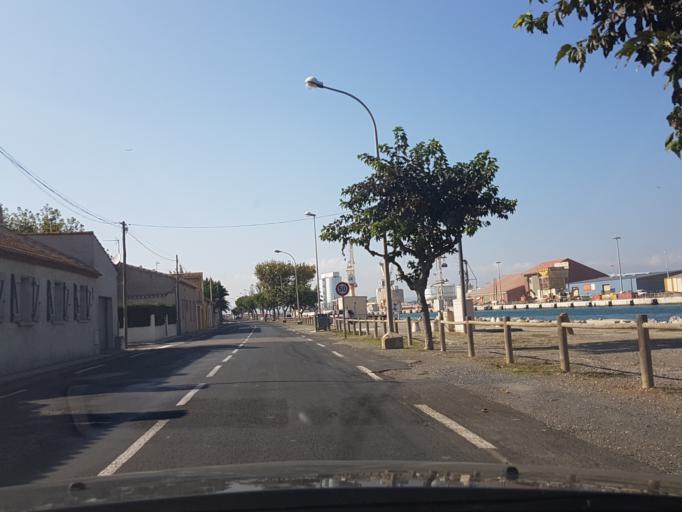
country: FR
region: Languedoc-Roussillon
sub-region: Departement de l'Aude
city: Port-la-Nouvelle
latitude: 43.0191
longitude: 3.0561
